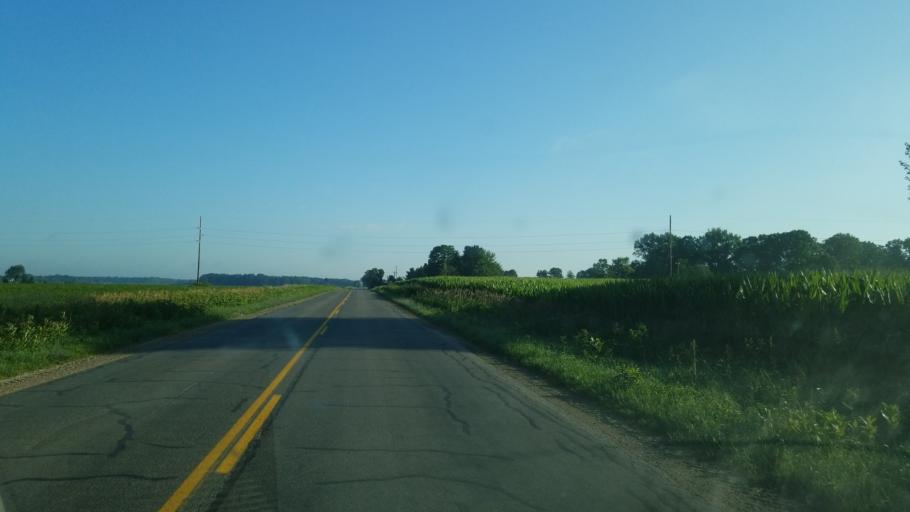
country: US
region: Michigan
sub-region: Montcalm County
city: Lakeview
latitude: 43.5190
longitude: -85.1847
